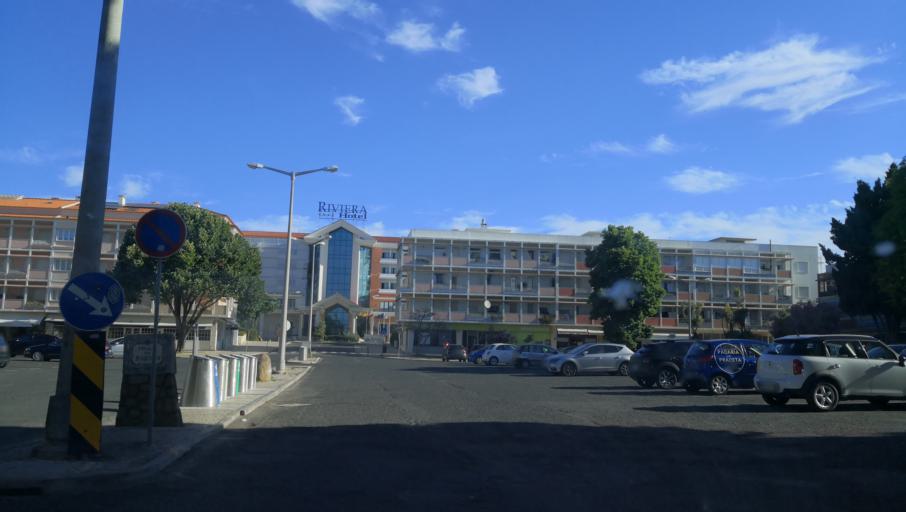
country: PT
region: Lisbon
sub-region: Cascais
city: Parede
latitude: 38.6837
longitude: -9.3426
